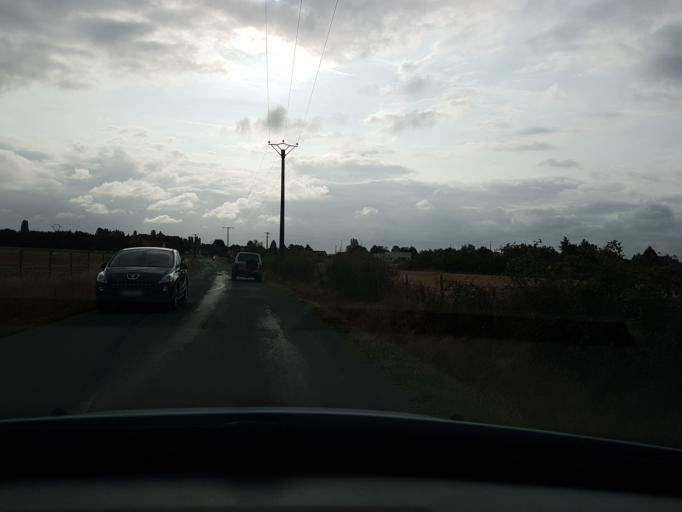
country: FR
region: Centre
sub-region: Departement d'Indre-et-Loire
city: Veretz
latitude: 47.3368
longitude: 0.8007
